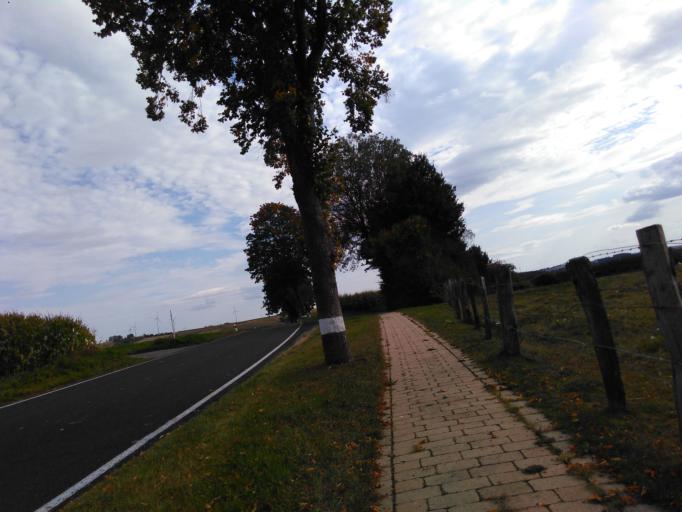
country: LU
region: Diekirch
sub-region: Canton de Clervaux
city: Troisvierges
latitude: 50.1392
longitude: 5.9848
